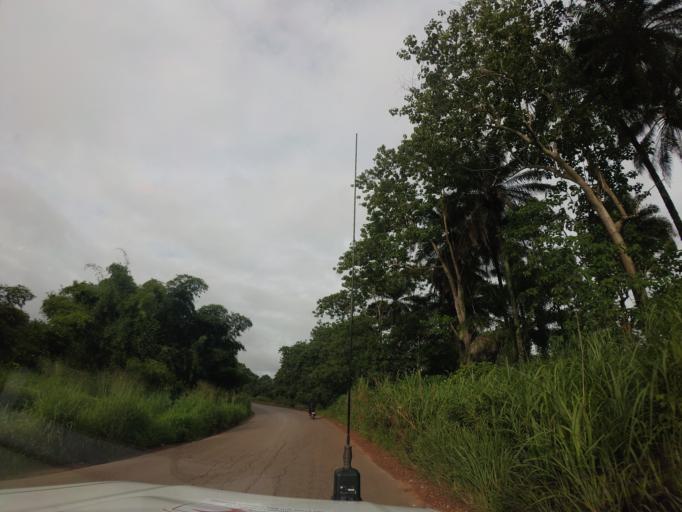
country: GN
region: Kindia
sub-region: Kindia
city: Kindia
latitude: 10.0018
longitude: -12.9048
